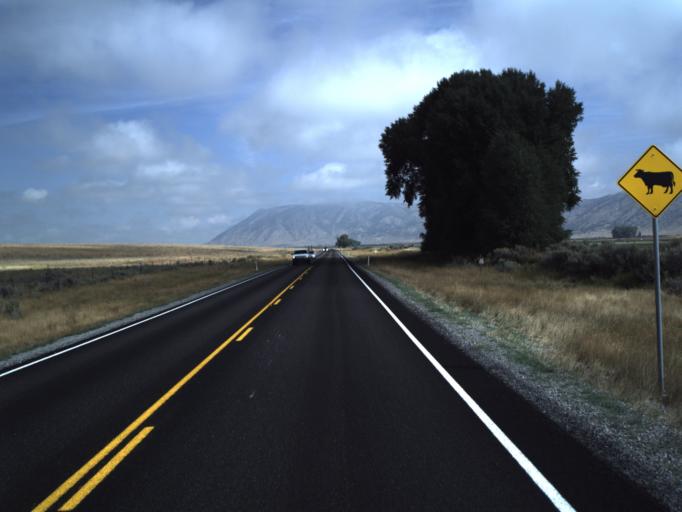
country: US
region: Utah
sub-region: Rich County
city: Randolph
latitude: 41.5426
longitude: -111.1585
